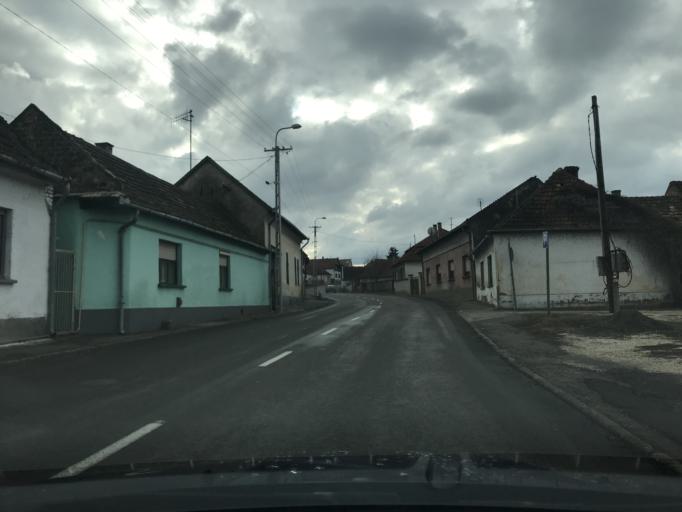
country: HU
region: Bacs-Kiskun
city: Csaszartoltes
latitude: 46.4204
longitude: 19.1757
